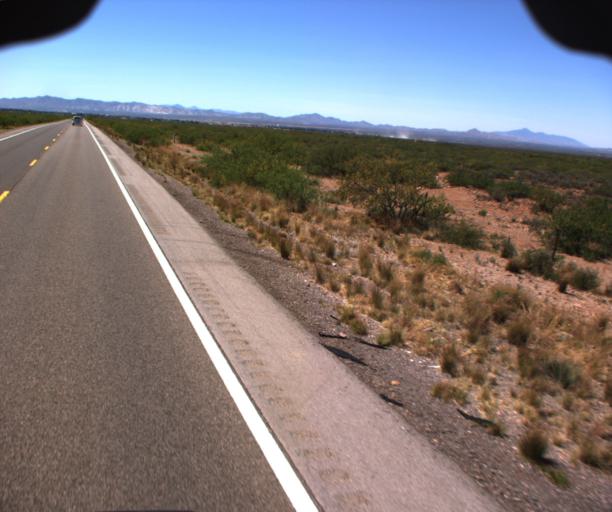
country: US
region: Arizona
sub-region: Cochise County
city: Douglas
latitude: 31.4013
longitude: -109.5041
